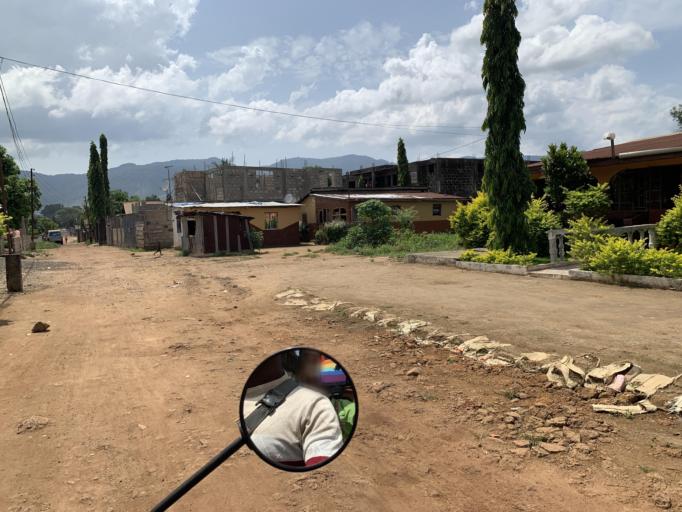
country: SL
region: Western Area
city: Hastings
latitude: 8.4000
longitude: -13.1385
